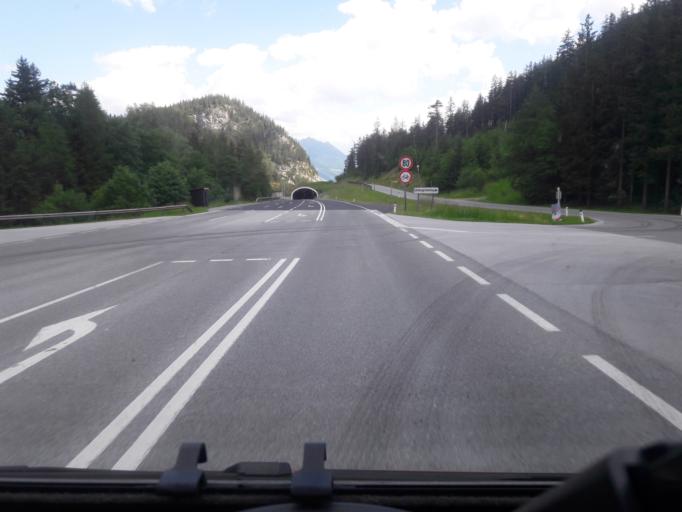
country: AT
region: Styria
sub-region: Politischer Bezirk Liezen
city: Tauplitz
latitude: 47.5349
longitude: 14.0507
